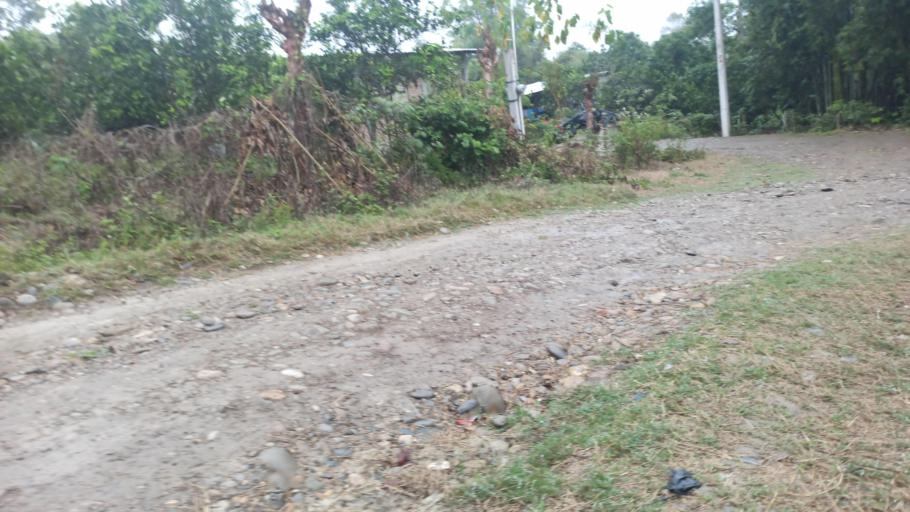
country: MX
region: Veracruz
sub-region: Papantla
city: El Chote
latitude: 20.3610
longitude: -97.3407
